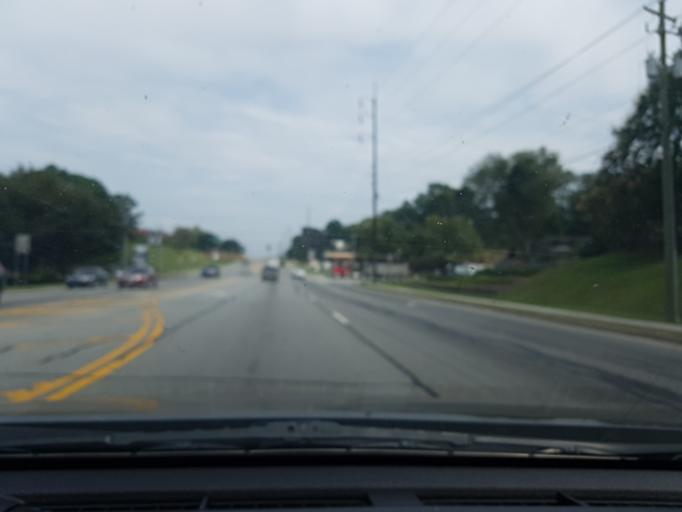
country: US
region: Georgia
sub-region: Gwinnett County
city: Lilburn
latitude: 33.9330
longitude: -84.1544
